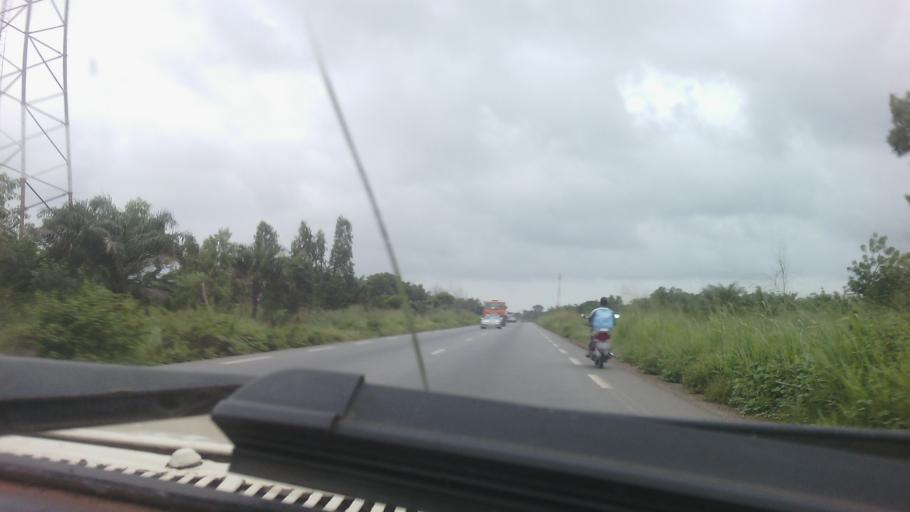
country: BJ
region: Atlantique
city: Ouidah
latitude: 6.3930
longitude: 1.9889
